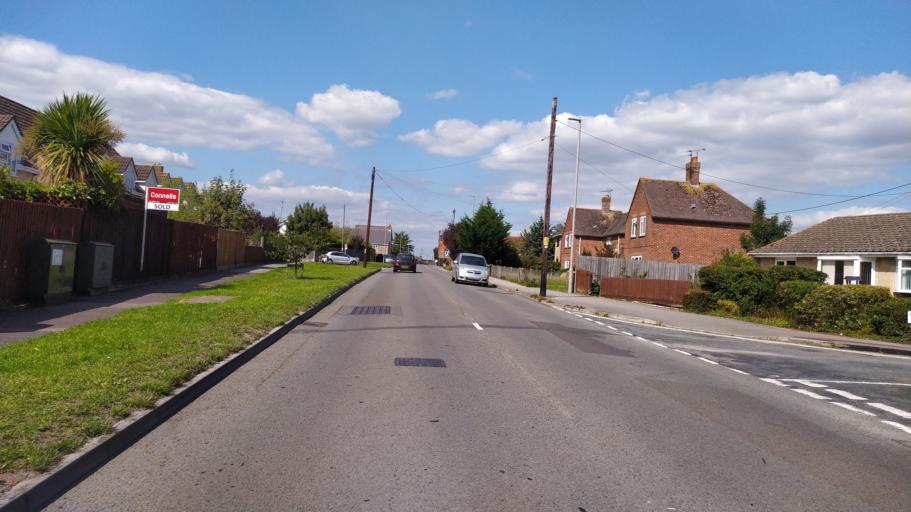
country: GB
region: England
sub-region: Dorset
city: Gillingham
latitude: 51.0445
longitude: -2.2790
